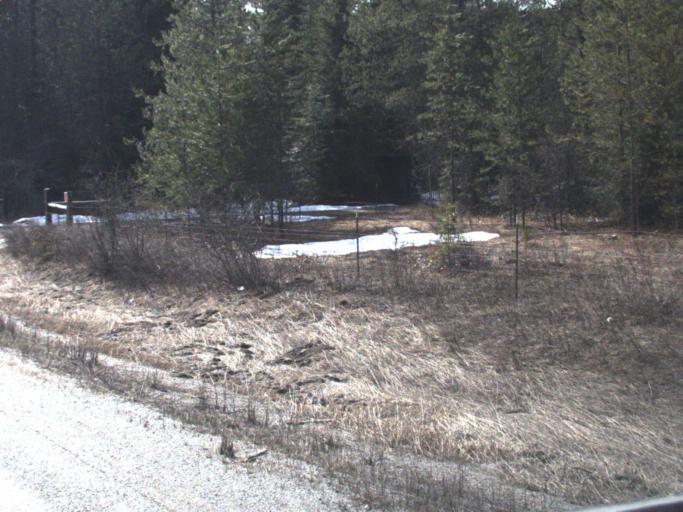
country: US
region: Washington
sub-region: Stevens County
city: Chewelah
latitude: 48.6393
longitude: -117.3716
